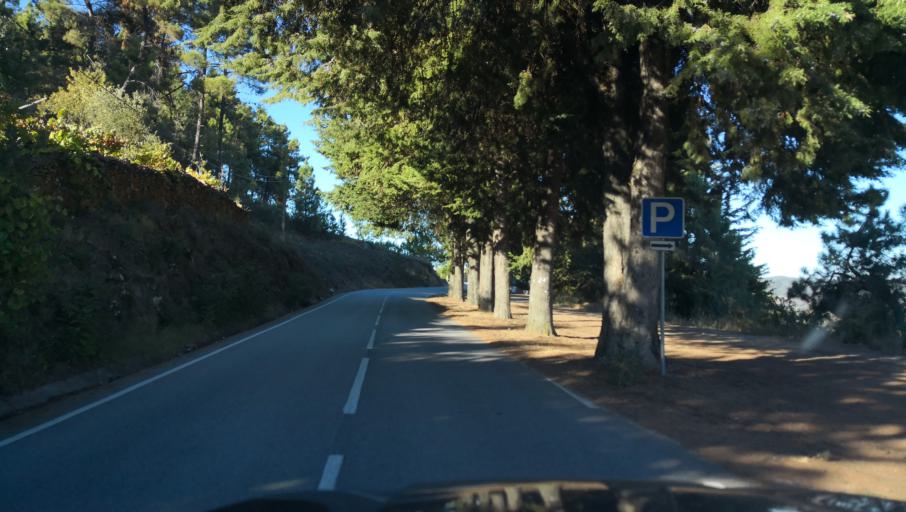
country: PT
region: Vila Real
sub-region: Sabrosa
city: Sabrosa
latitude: 41.2728
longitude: -7.5683
